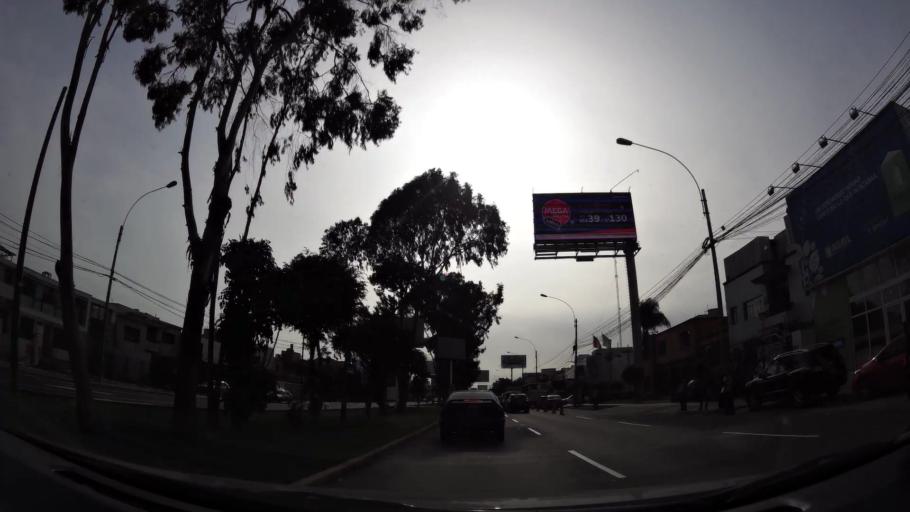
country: PE
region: Lima
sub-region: Lima
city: San Isidro
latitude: -12.0890
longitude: -77.0591
